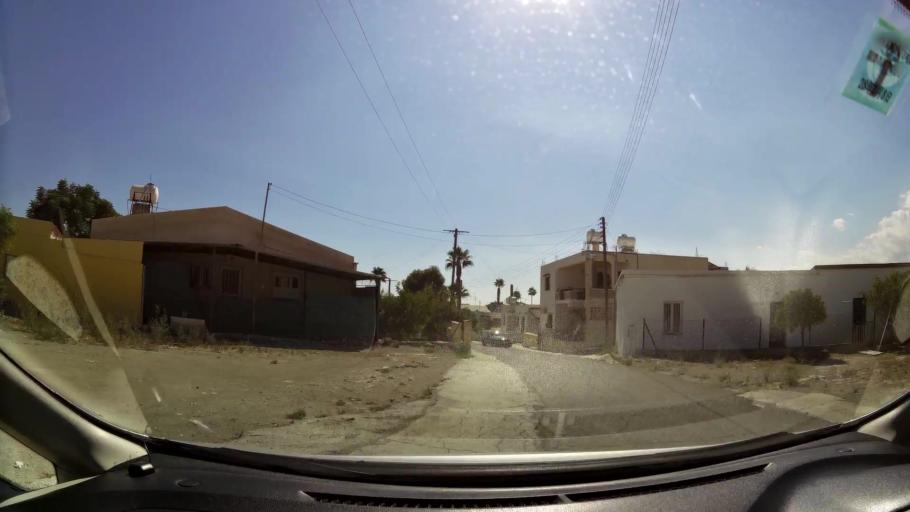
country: CY
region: Larnaka
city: Livadia
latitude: 34.9579
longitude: 33.6245
